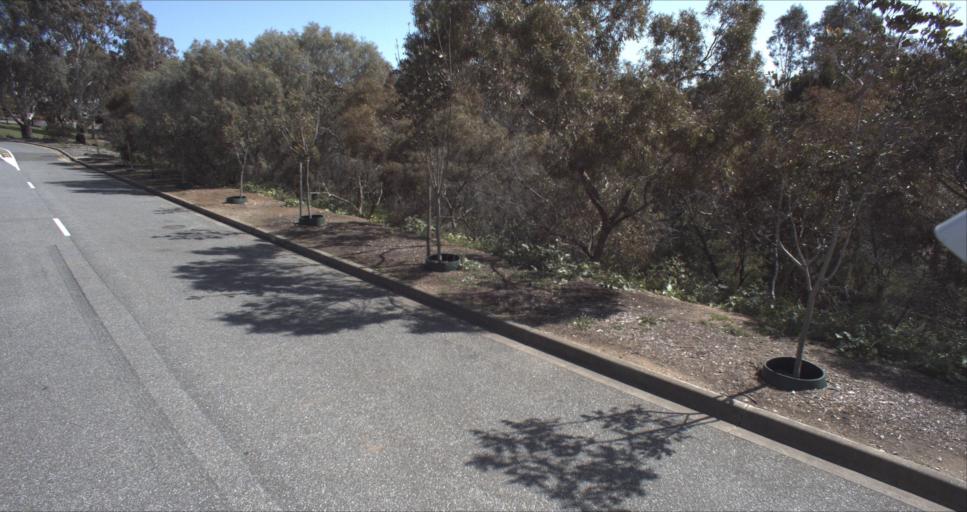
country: AU
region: South Australia
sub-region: Port Adelaide Enfield
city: Gilles Plains
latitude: -34.8435
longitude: 138.6459
